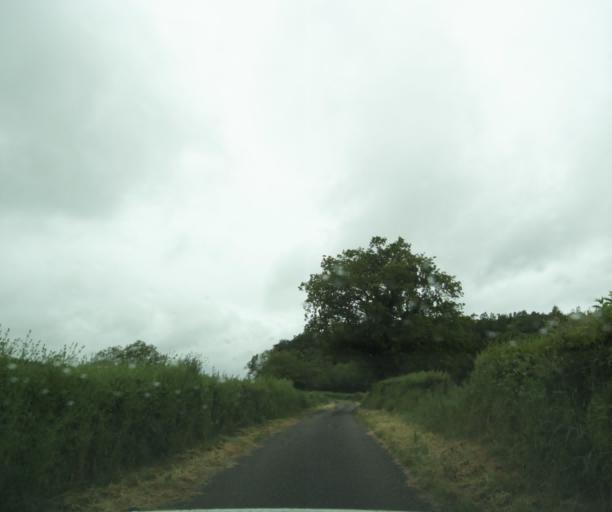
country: FR
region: Bourgogne
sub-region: Departement de Saone-et-Loire
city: Saint-Vallier
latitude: 46.4979
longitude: 4.4586
